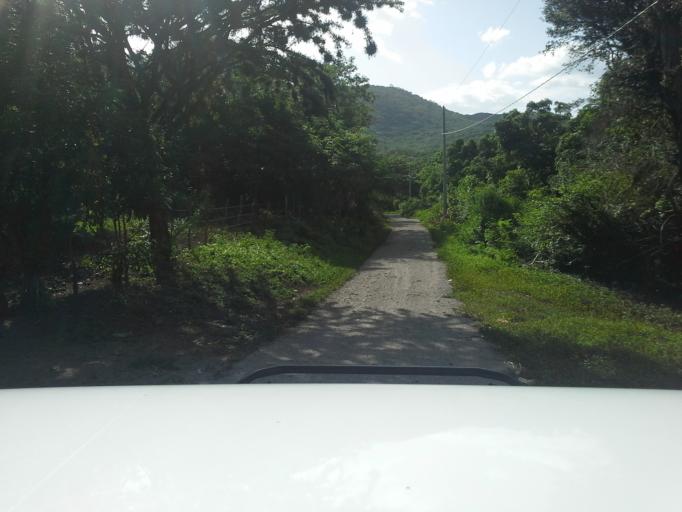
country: NI
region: Matagalpa
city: Ciudad Dario
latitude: 12.6715
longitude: -86.0515
